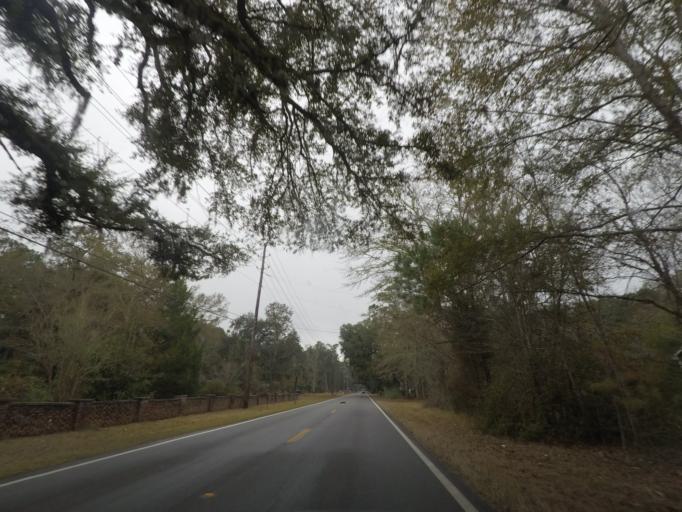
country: US
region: South Carolina
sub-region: Charleston County
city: Hollywood
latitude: 32.7168
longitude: -80.3492
